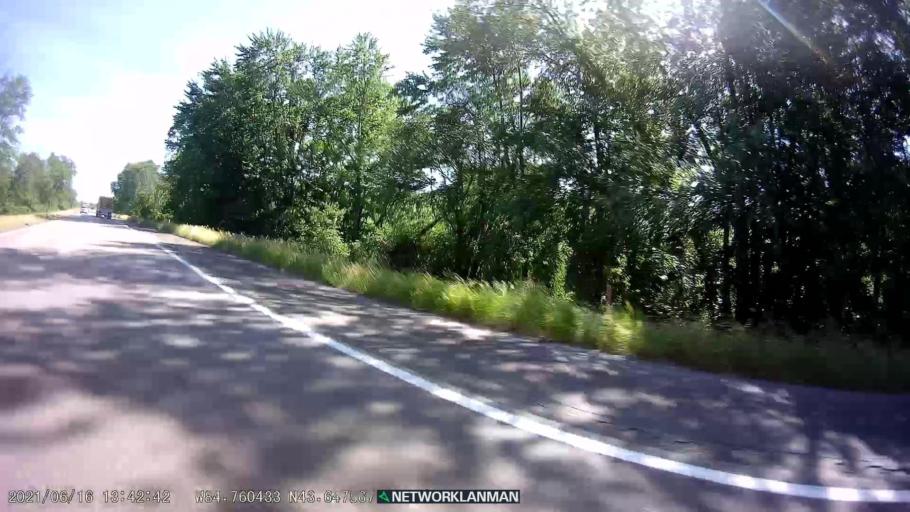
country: US
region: Michigan
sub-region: Isabella County
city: Mount Pleasant
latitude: 43.6473
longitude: -84.7603
